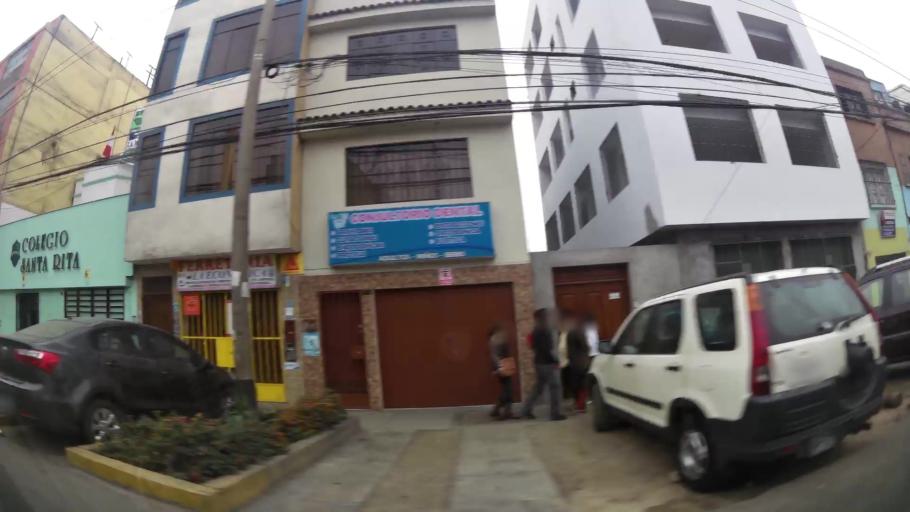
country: PE
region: Lima
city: Lima
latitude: -12.0735
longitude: -77.0477
